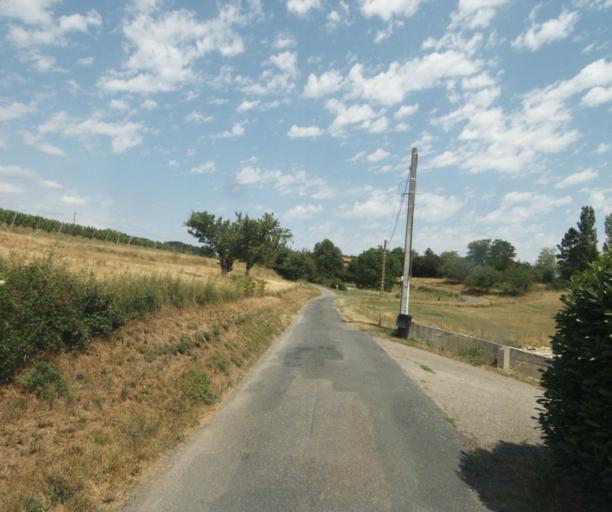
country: FR
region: Rhone-Alpes
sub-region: Departement du Rhone
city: Saint-Germain-Nuelles
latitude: 45.8512
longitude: 4.6307
